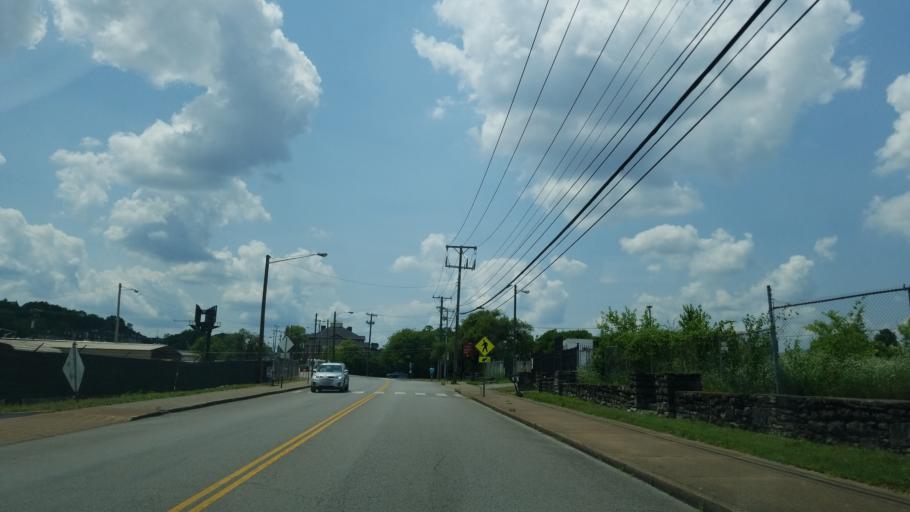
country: US
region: Tennessee
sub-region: Davidson County
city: Nashville
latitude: 36.1422
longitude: -86.7740
